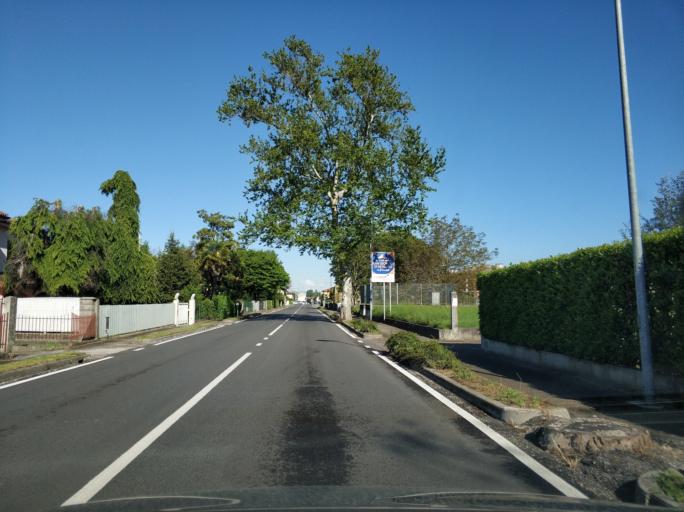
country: IT
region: Friuli Venezia Giulia
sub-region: Provincia di Udine
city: San Giorgio di Nogaro
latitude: 45.8295
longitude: 13.2251
